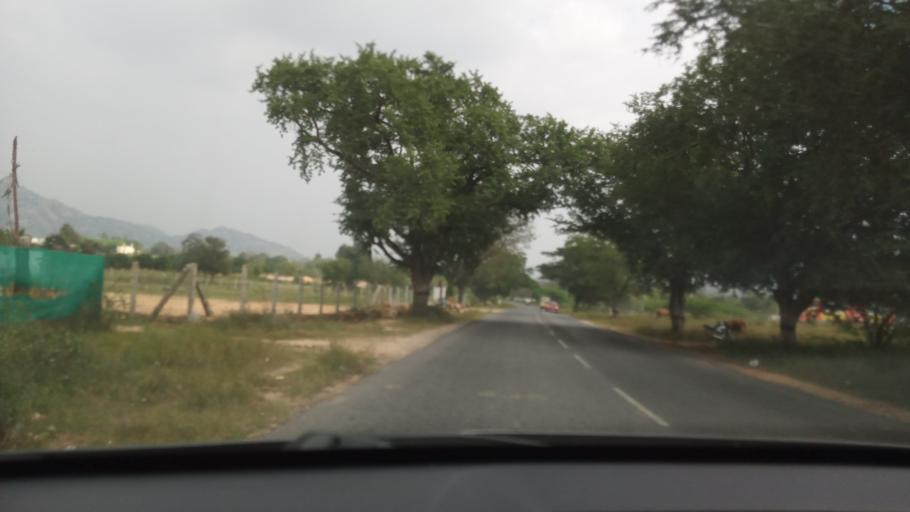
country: IN
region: Andhra Pradesh
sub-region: Chittoor
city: Madanapalle
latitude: 13.6518
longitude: 78.8202
